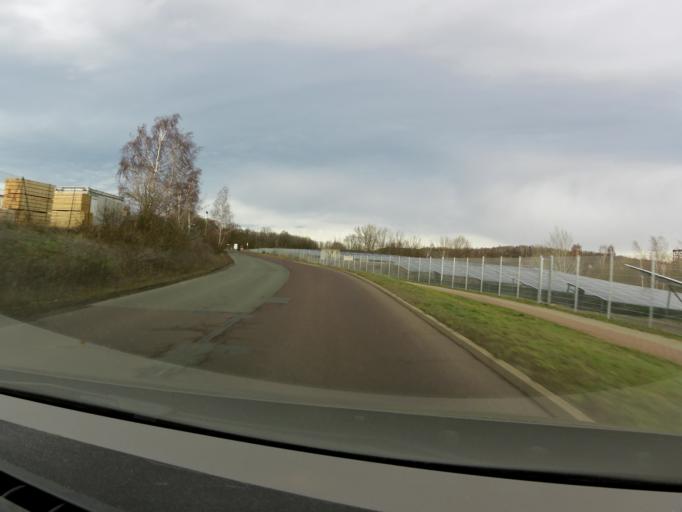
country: DE
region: Saxony-Anhalt
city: Grossorner
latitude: 51.6228
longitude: 11.5028
